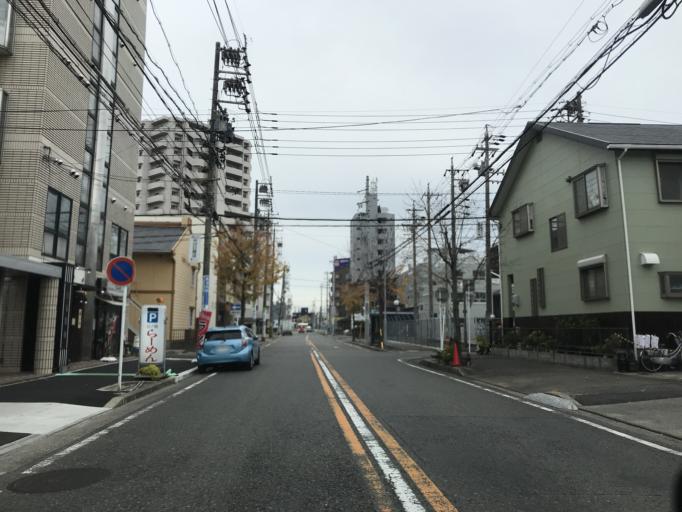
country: JP
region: Aichi
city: Nagoya-shi
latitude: 35.1757
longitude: 136.8636
